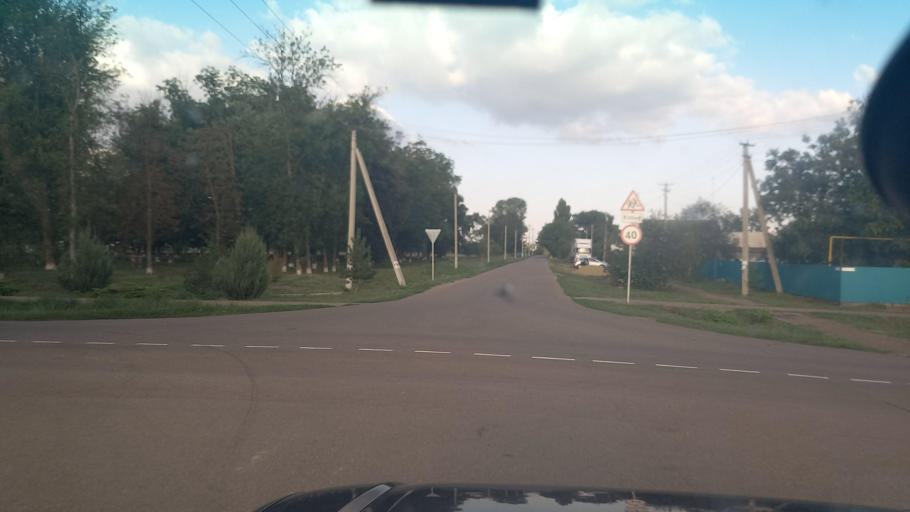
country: RU
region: Adygeya
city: Khatukay
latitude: 45.2942
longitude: 39.5607
